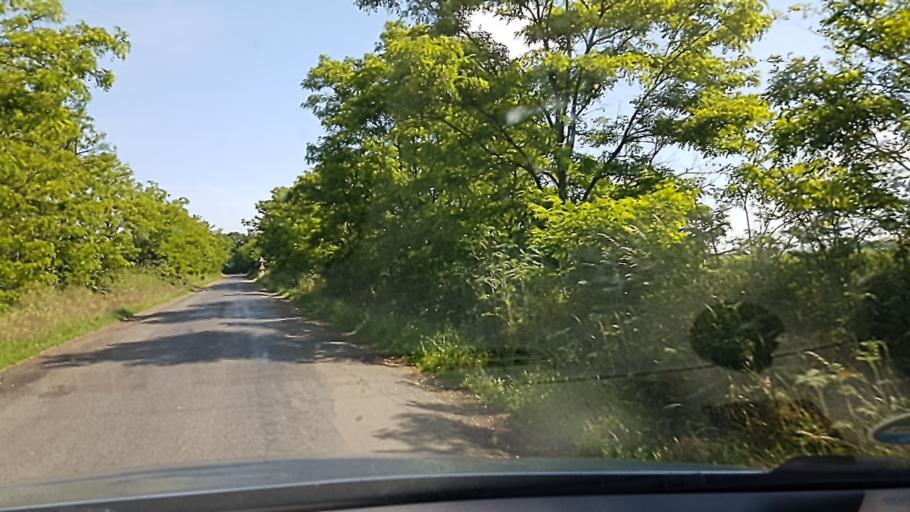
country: HU
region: Borsod-Abauj-Zemplen
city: Harsany
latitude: 47.9236
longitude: 20.7165
